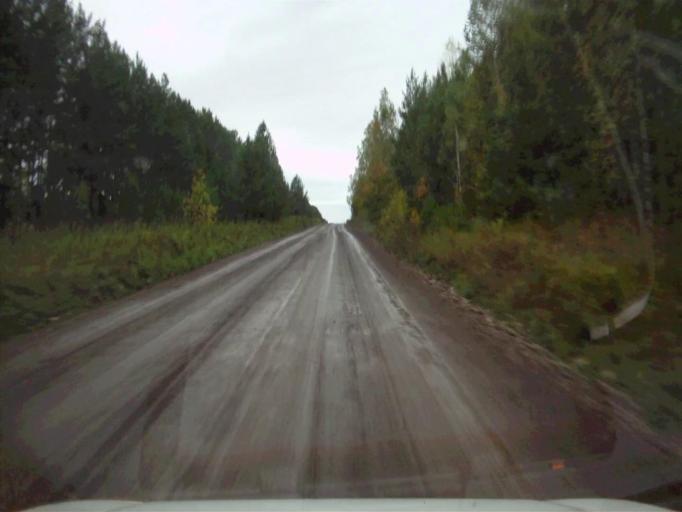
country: RU
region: Chelyabinsk
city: Nyazepetrovsk
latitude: 56.1421
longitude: 59.2904
